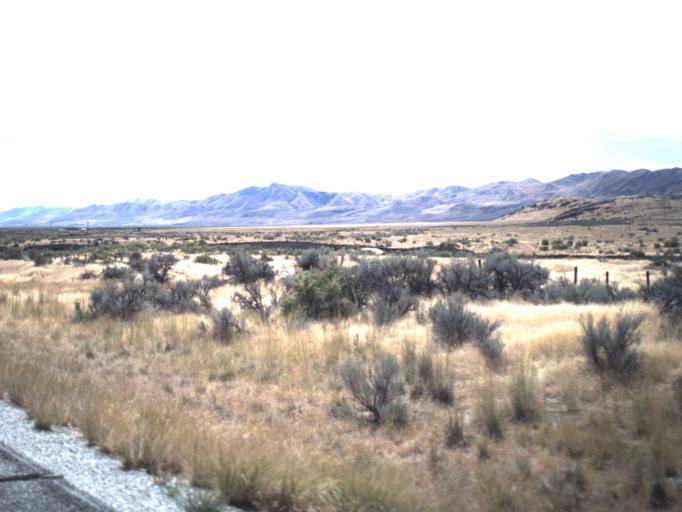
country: US
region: Utah
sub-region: Box Elder County
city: Tremonton
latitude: 41.6693
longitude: -112.4465
